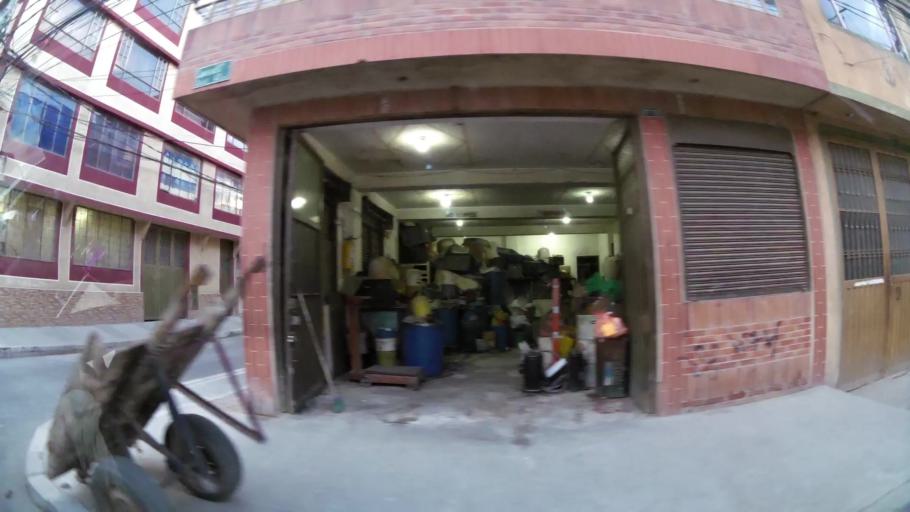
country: CO
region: Cundinamarca
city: Soacha
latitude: 4.6246
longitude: -74.1633
